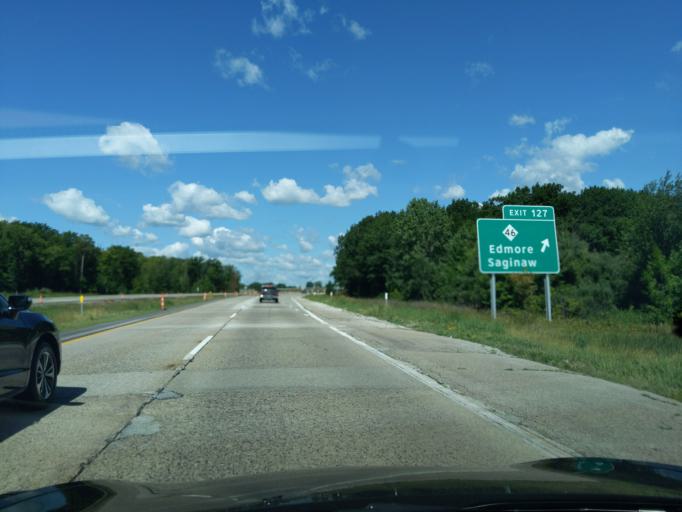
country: US
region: Michigan
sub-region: Gratiot County
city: Alma
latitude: 43.4044
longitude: -84.6535
